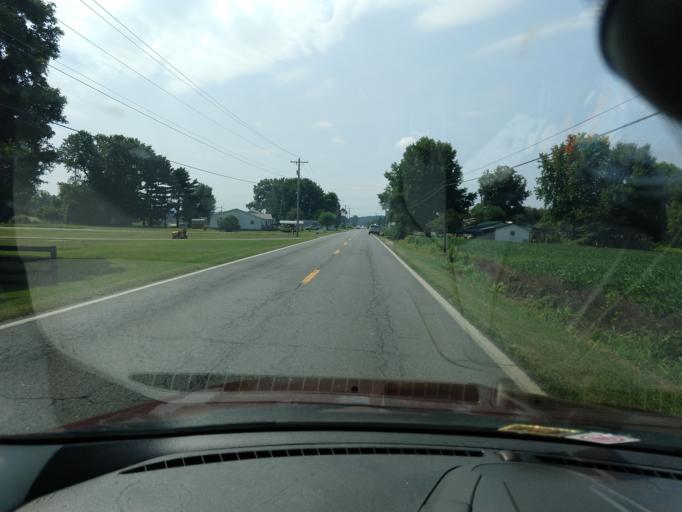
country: US
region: West Virginia
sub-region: Mason County
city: New Haven
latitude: 38.9539
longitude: -81.9223
